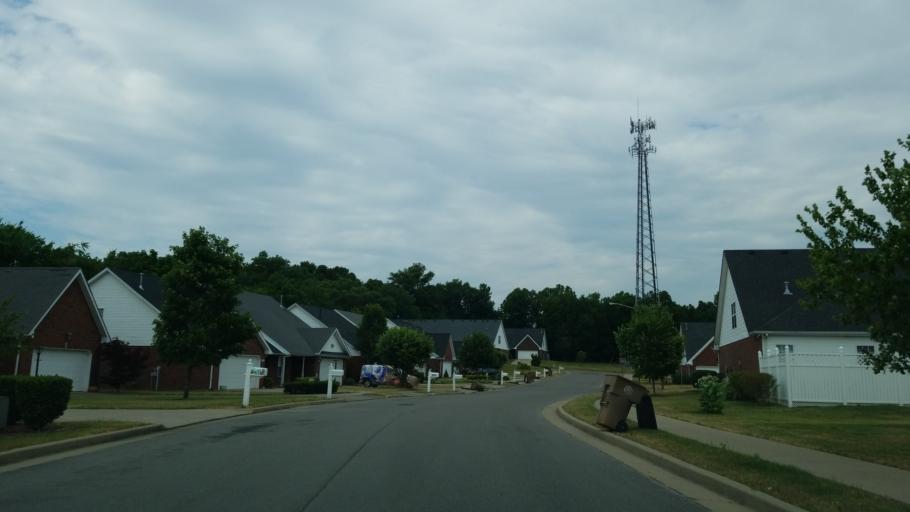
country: US
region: Tennessee
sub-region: Rutherford County
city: La Vergne
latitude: 36.0339
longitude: -86.5928
